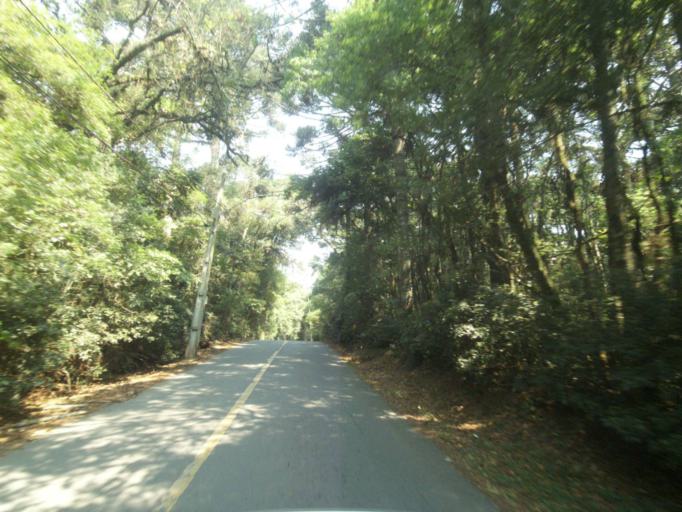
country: BR
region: Parana
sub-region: Sao Jose Dos Pinhais
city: Sao Jose dos Pinhais
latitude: -25.5529
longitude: -49.2336
